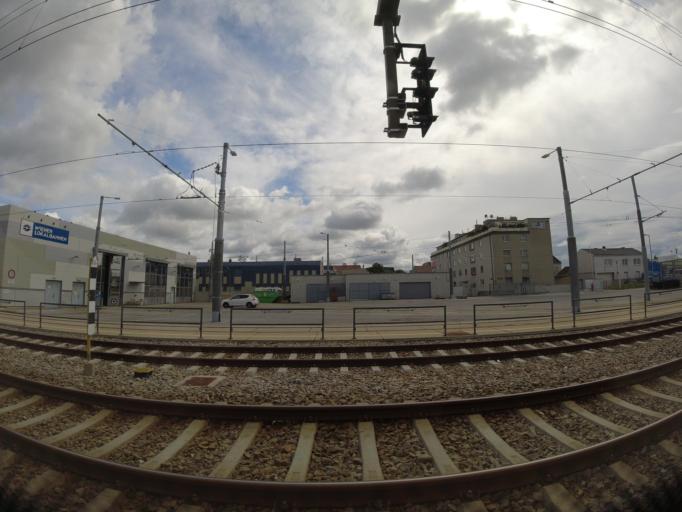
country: AT
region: Lower Austria
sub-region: Politischer Bezirk Modling
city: Vosendorf
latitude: 48.1462
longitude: 16.3313
